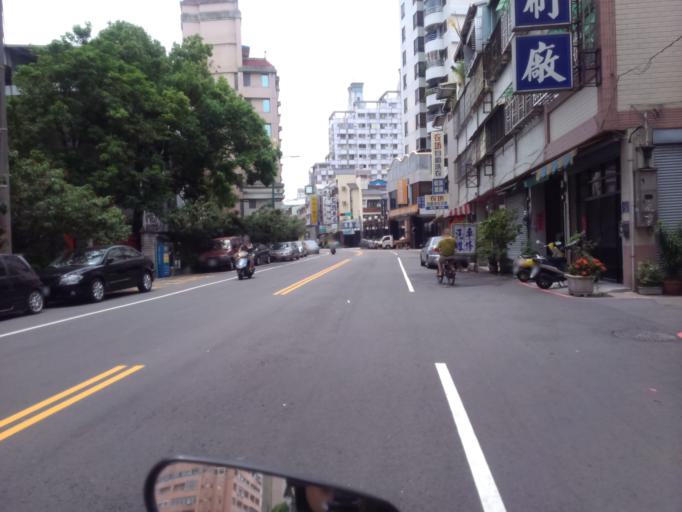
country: TW
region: Taiwan
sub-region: Taichung City
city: Taichung
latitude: 24.1678
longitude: 120.6755
